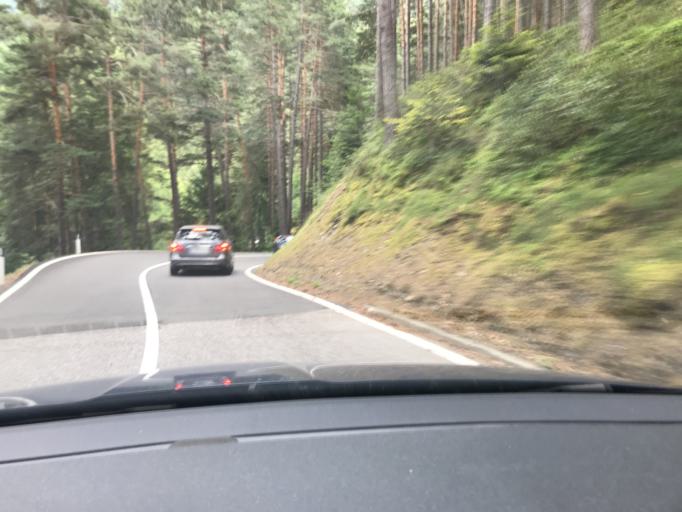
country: IT
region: Trentino-Alto Adige
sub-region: Bolzano
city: Bressanone
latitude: 46.6936
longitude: 11.6815
